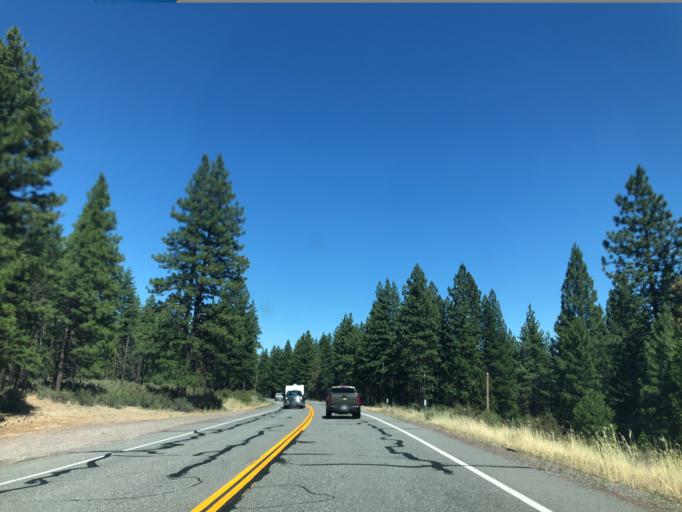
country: US
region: California
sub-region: Lassen County
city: Susanville
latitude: 40.4149
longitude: -120.7271
